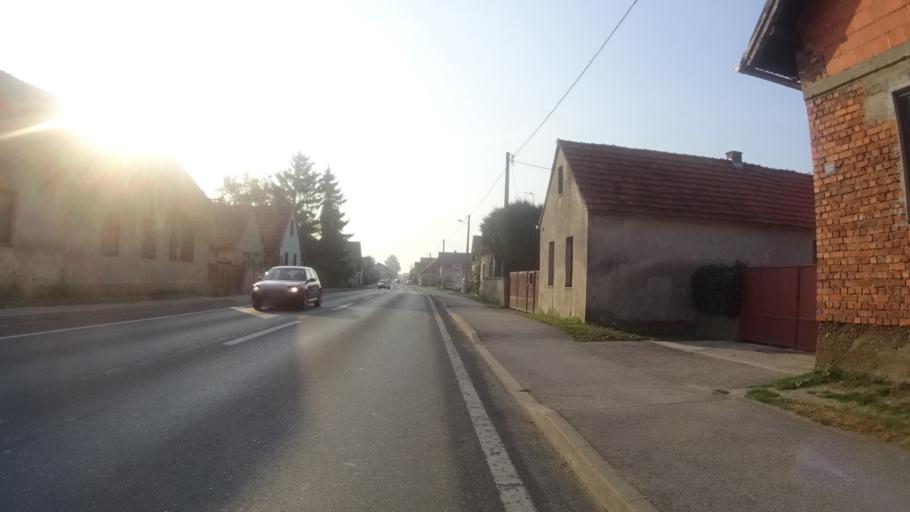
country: HR
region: Varazdinska
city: Petrijanec
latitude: 46.3458
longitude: 16.2277
